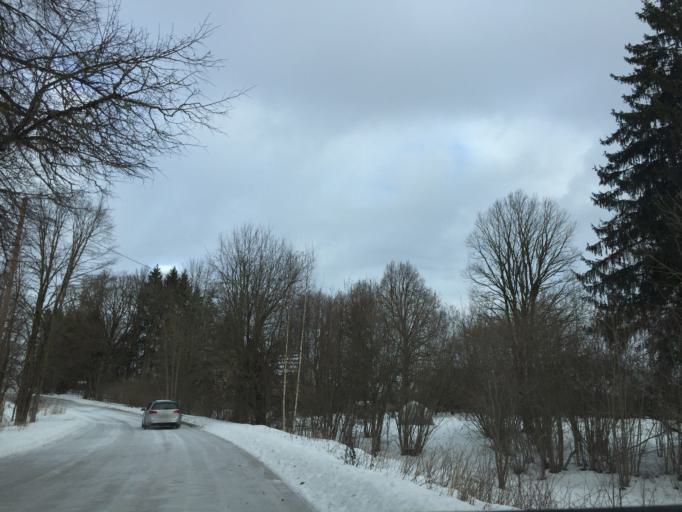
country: LV
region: Lielvarde
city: Lielvarde
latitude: 56.5757
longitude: 24.7369
